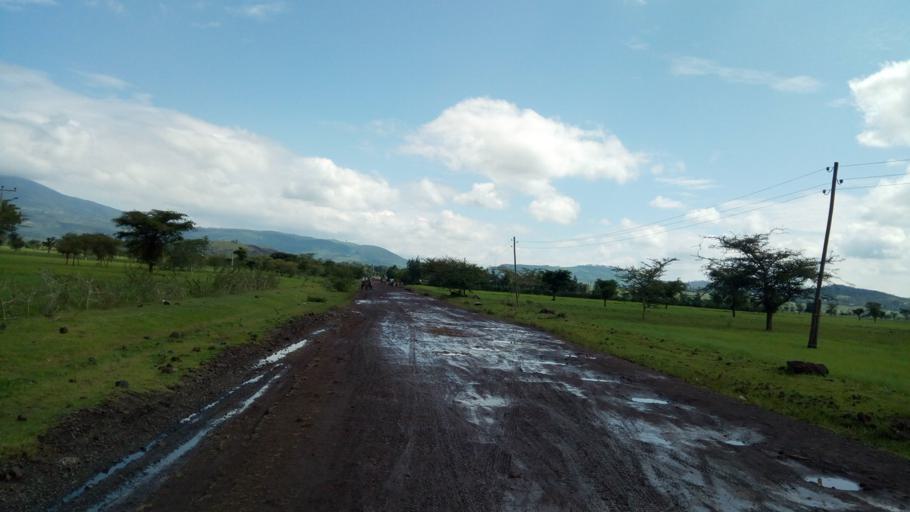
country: ET
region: Oromiya
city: Bishoftu
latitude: 8.8135
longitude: 39.0047
